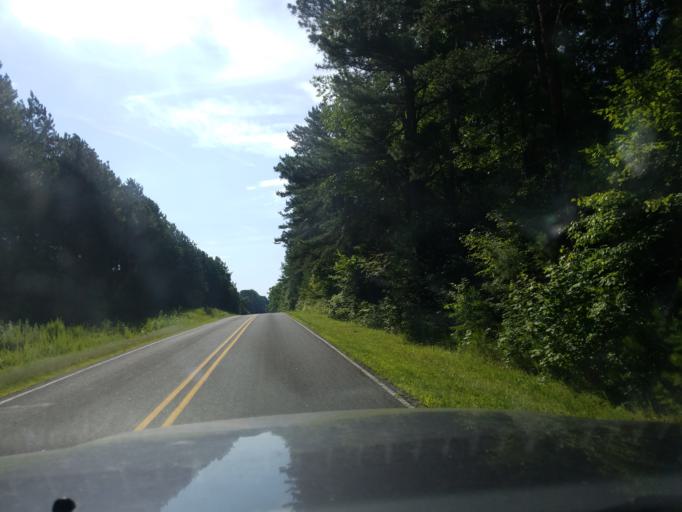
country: US
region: North Carolina
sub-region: Granville County
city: Butner
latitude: 36.1847
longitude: -78.8189
